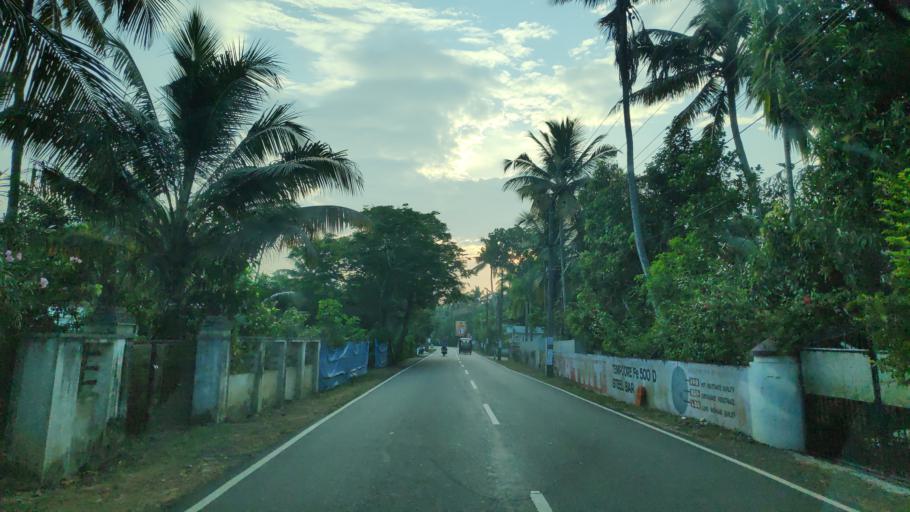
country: IN
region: Kerala
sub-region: Alappuzha
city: Shertallai
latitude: 9.6780
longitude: 76.3860
